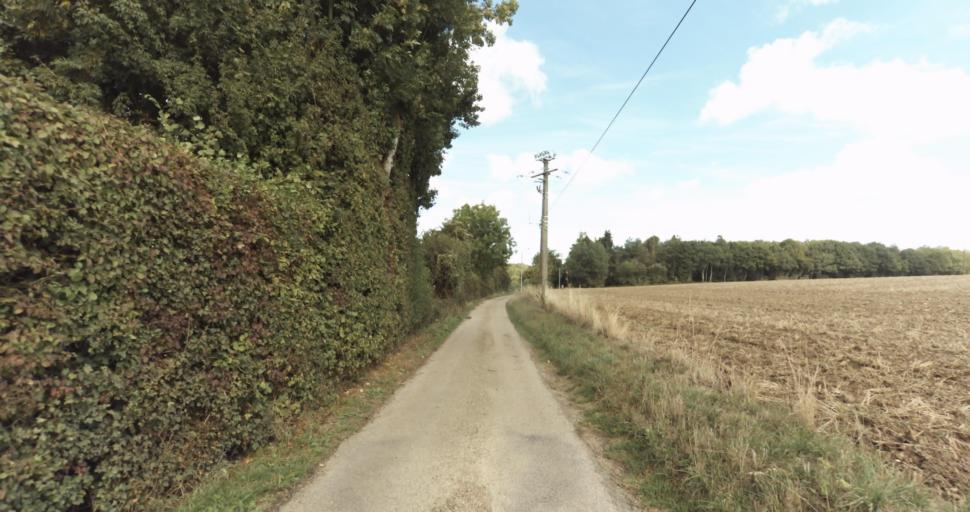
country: FR
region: Lower Normandy
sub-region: Departement de l'Orne
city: Gace
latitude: 48.8938
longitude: 0.3636
